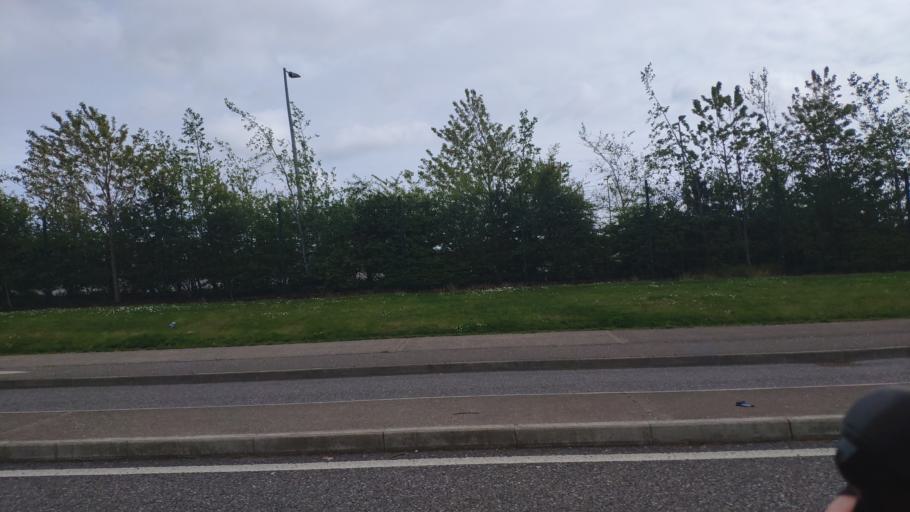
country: IE
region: Munster
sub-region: County Cork
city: Cork
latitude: 51.9077
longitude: -8.5162
